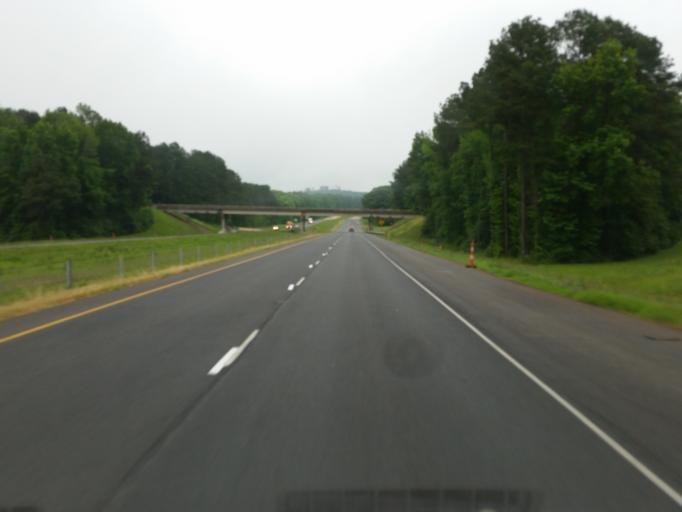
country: US
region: Louisiana
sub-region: Bienville Parish
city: Arcadia
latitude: 32.5633
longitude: -93.0568
